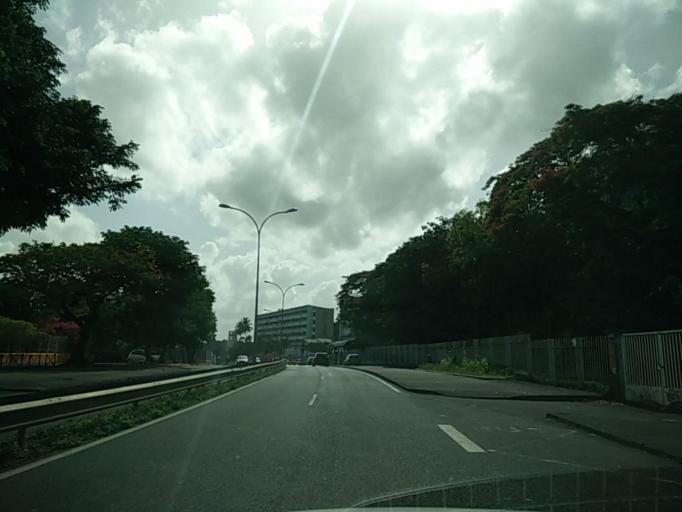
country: GP
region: Guadeloupe
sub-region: Guadeloupe
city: Pointe-a-Pitre
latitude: 16.2485
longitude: -61.5256
